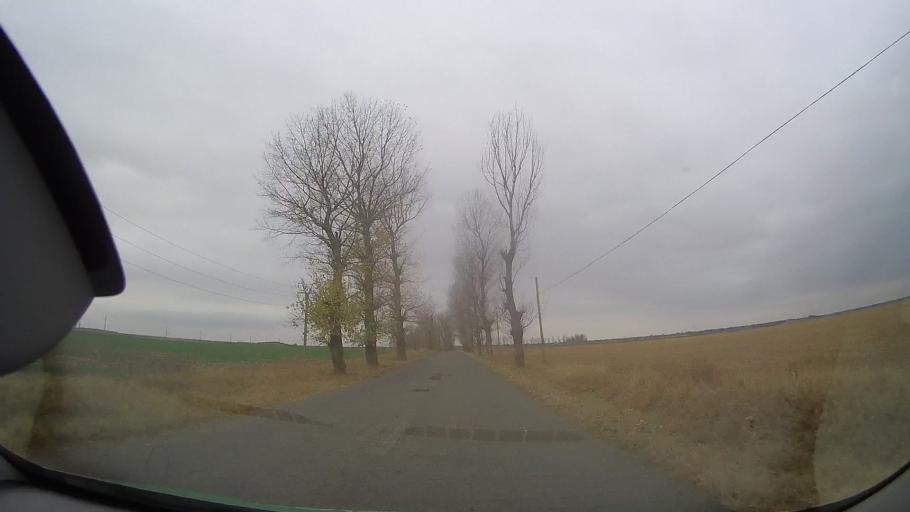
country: RO
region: Buzau
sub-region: Comuna Rusetu
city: Rusetu
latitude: 44.9422
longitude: 27.2428
